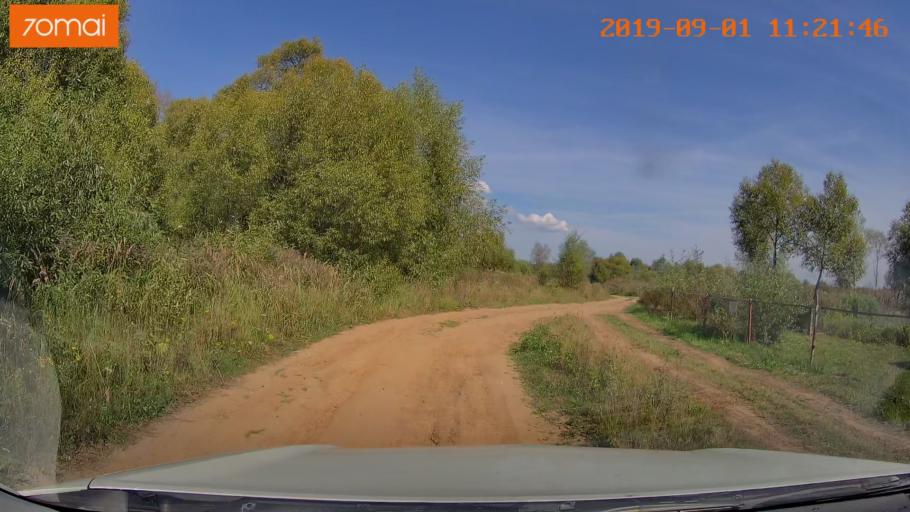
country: RU
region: Kaluga
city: Detchino
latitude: 54.8314
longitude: 36.3599
